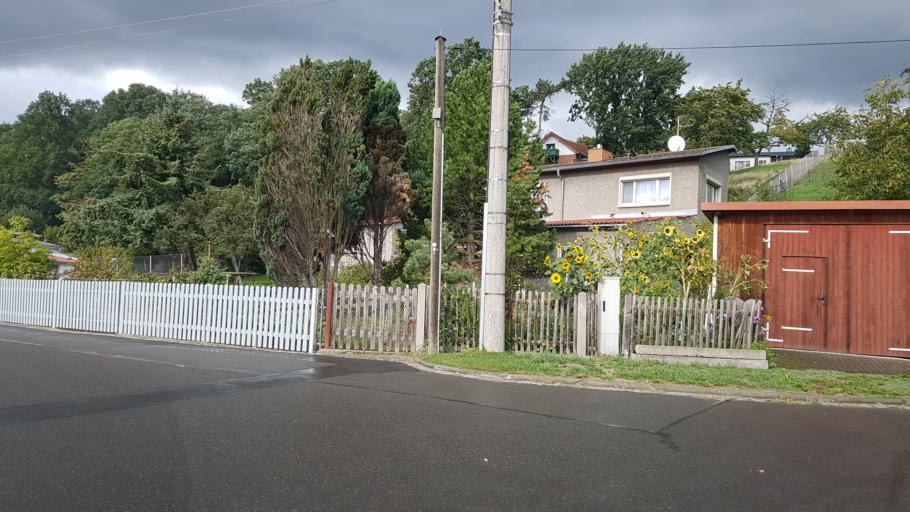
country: DE
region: Saxony
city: Dahlen
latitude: 51.3670
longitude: 13.0072
